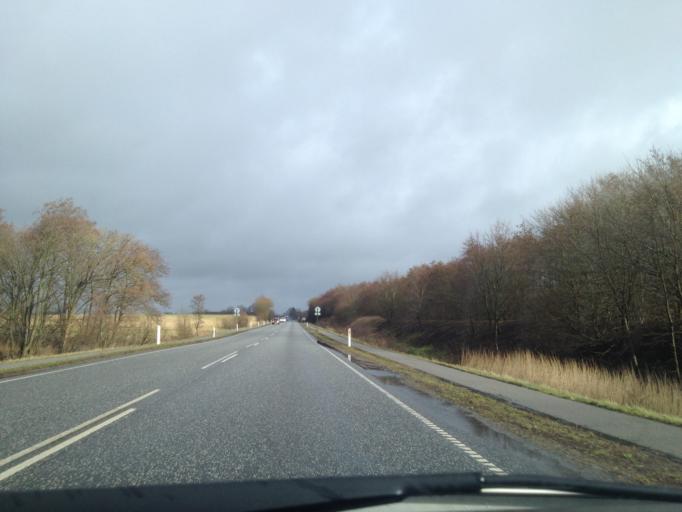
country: DK
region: South Denmark
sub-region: Kolding Kommune
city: Lunderskov
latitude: 55.4471
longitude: 9.3583
